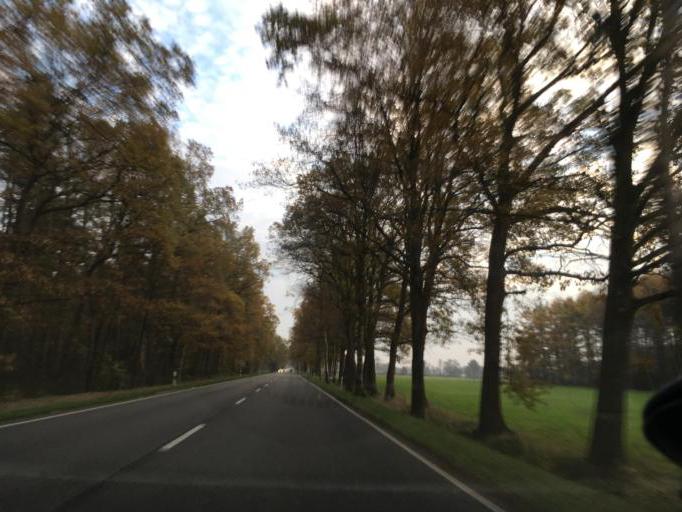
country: DE
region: Lower Saxony
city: Winsen
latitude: 52.7160
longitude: 9.9739
